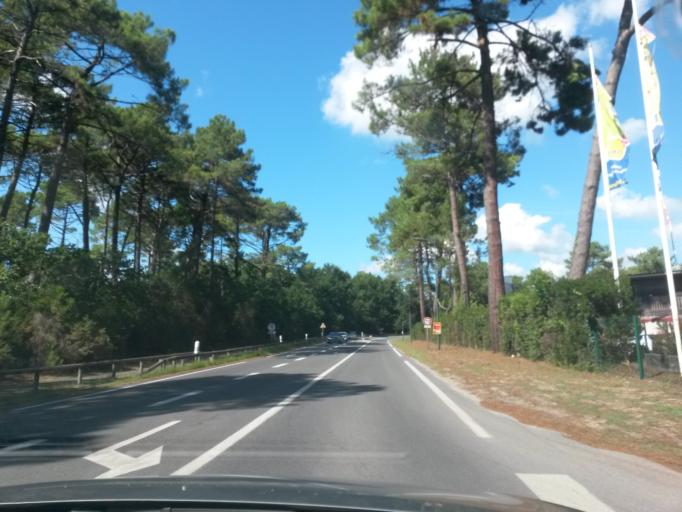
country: FR
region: Aquitaine
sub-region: Departement de la Gironde
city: Ares
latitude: 44.7342
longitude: -1.1965
